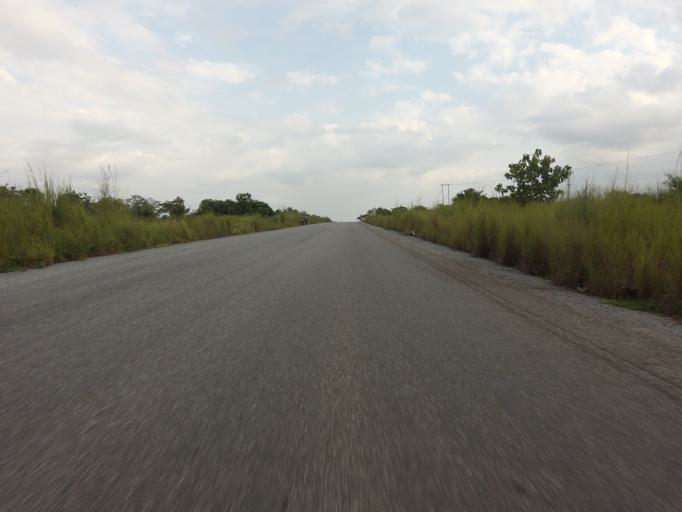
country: GH
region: Volta
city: Ho
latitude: 6.4137
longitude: 0.5213
